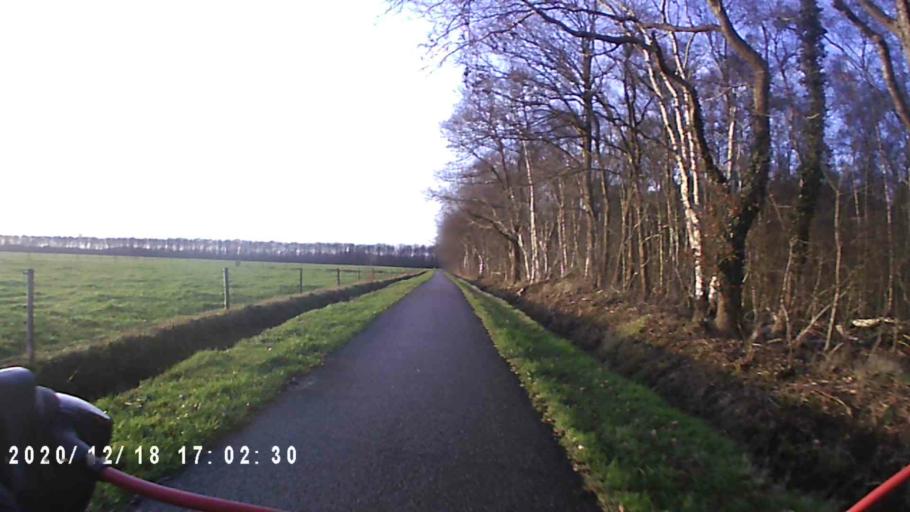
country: NL
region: Drenthe
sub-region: Gemeente Tynaarlo
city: Tynaarlo
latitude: 53.0635
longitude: 6.6352
